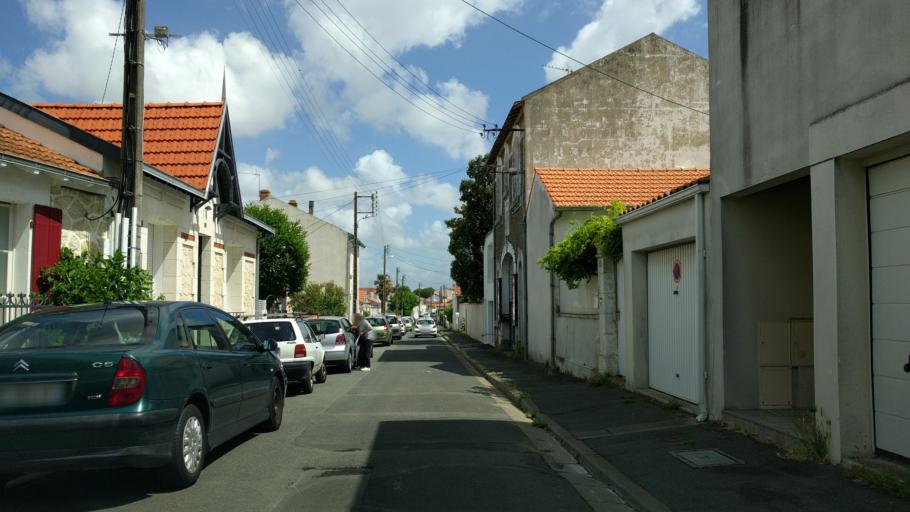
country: FR
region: Poitou-Charentes
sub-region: Departement de la Charente-Maritime
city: La Rochelle
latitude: 46.1690
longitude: -1.1439
